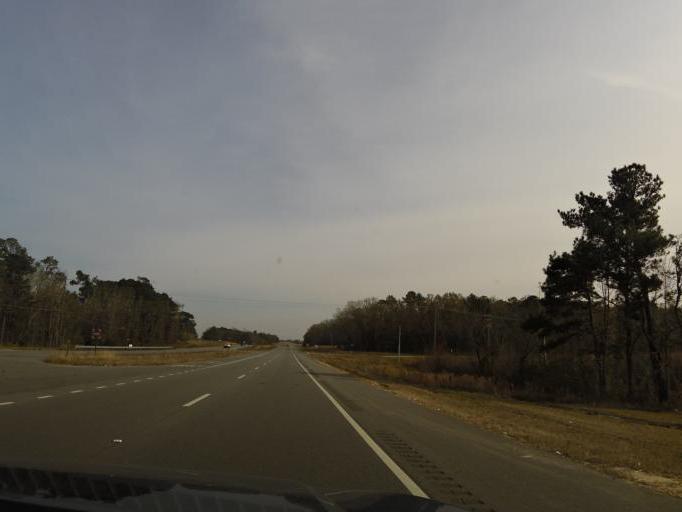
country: US
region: Alabama
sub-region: Houston County
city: Cowarts
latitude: 31.1869
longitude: -85.2727
